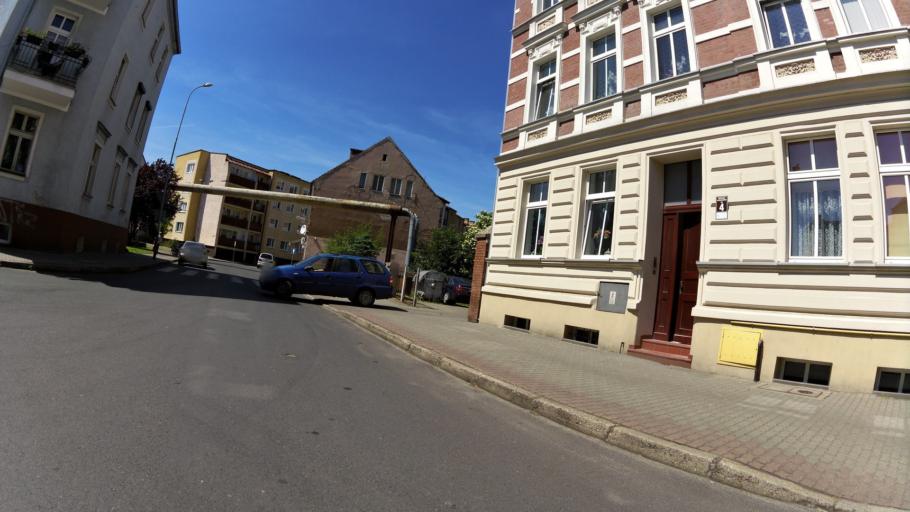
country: PL
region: Lubusz
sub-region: Powiat slubicki
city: Slubice
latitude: 52.3512
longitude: 14.5647
